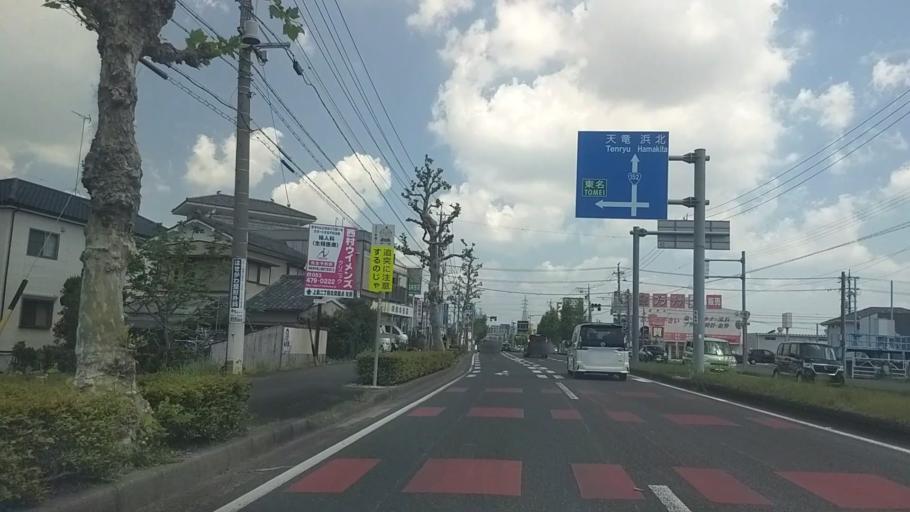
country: JP
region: Shizuoka
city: Hamamatsu
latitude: 34.7311
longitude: 137.7334
